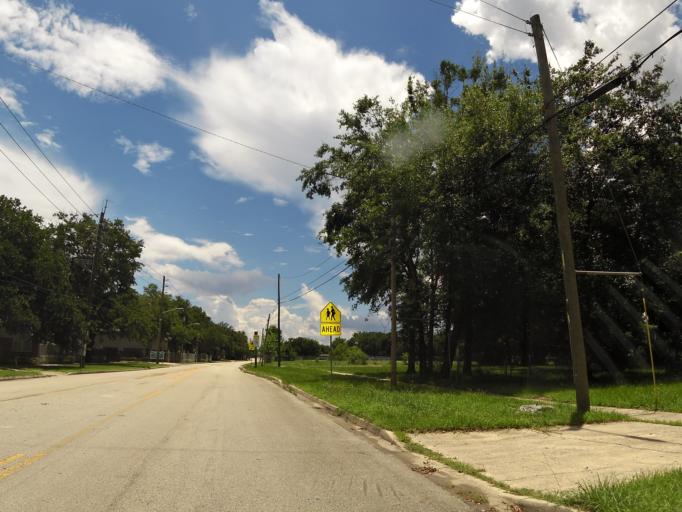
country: US
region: Florida
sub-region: Duval County
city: Jacksonville
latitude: 30.3410
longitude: -81.6669
